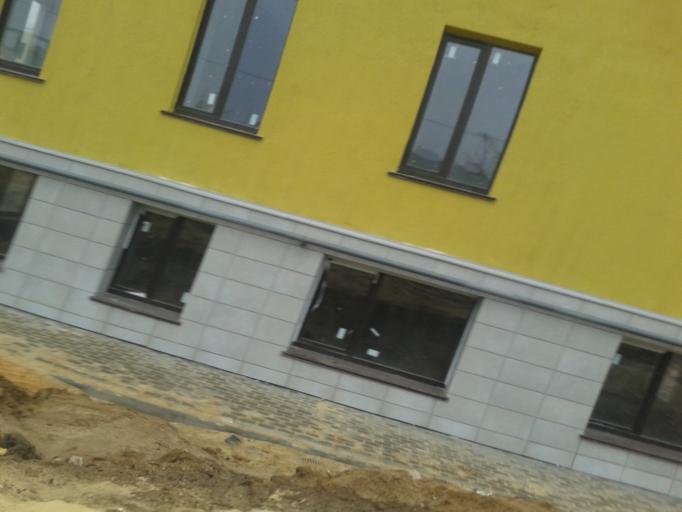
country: RU
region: Volgograd
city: Volgograd
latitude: 48.6641
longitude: 44.4094
